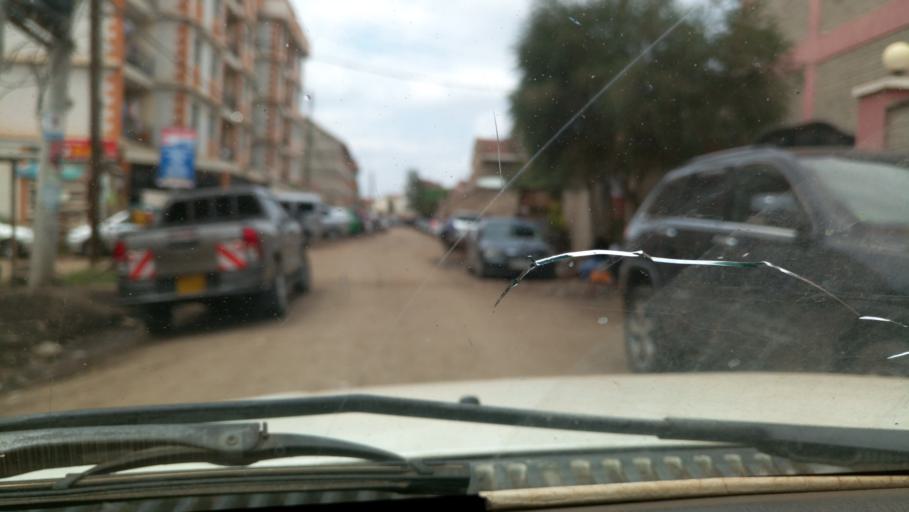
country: KE
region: Nairobi Area
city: Pumwani
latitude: -1.3209
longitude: 36.8458
